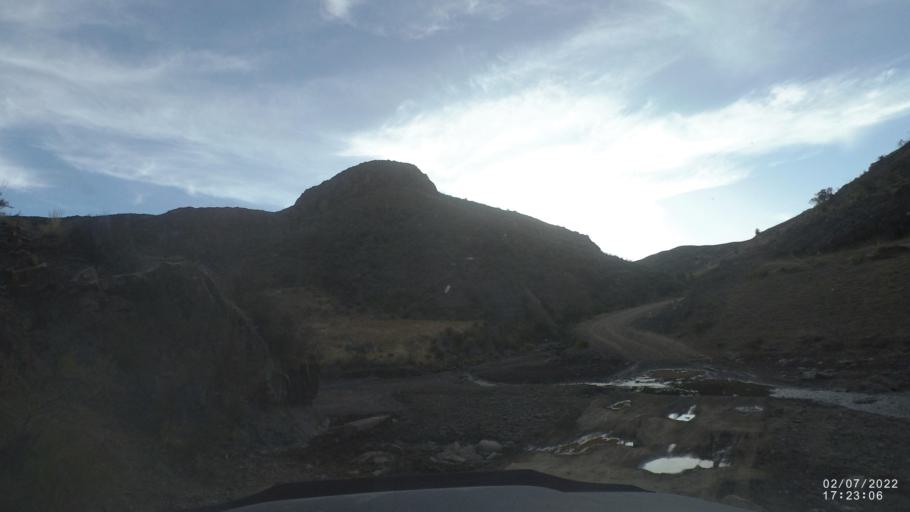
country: BO
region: Cochabamba
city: Irpa Irpa
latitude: -17.8785
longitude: -66.5986
